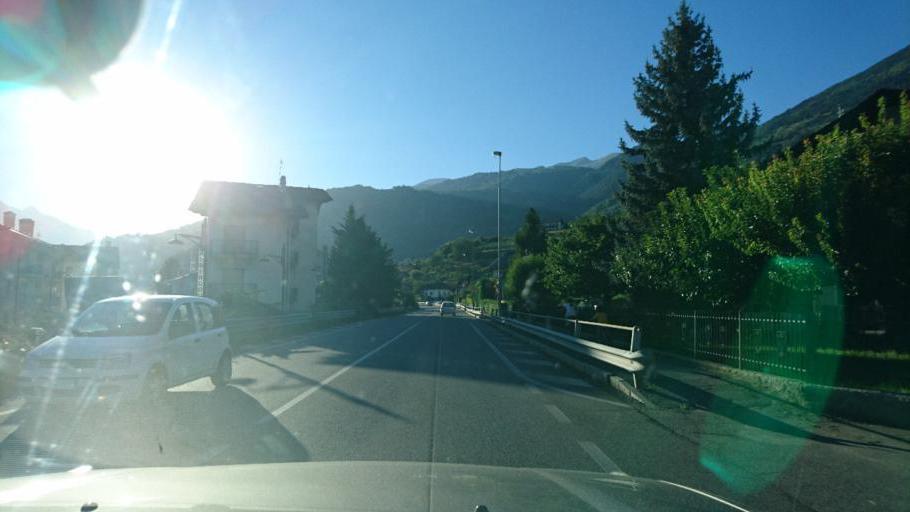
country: IT
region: Aosta Valley
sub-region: Valle d'Aosta
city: Saint-Pierre
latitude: 45.7092
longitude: 7.2344
